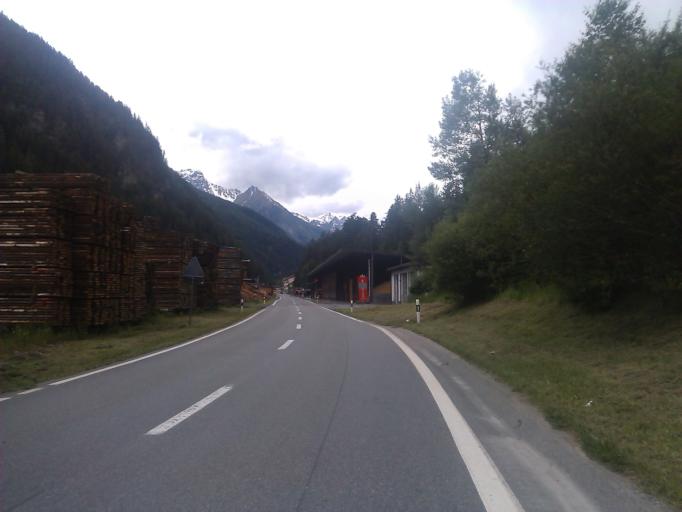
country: AT
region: Tyrol
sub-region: Politischer Bezirk Landeck
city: Nauders
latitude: 46.8890
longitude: 10.4679
